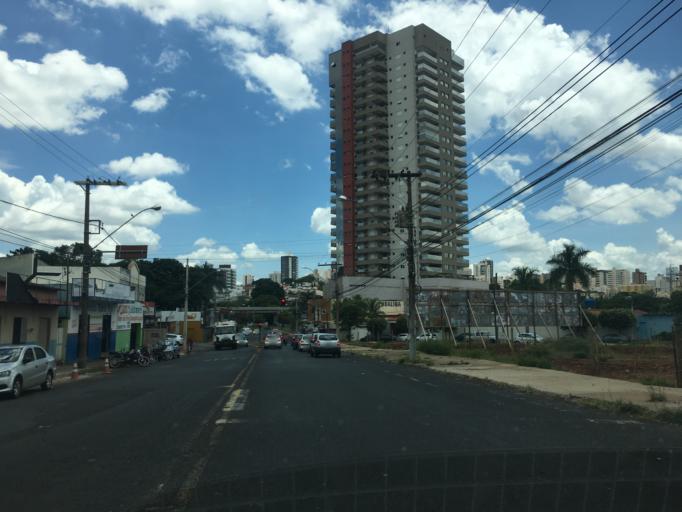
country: BR
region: Minas Gerais
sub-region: Uberlandia
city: Uberlandia
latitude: -18.9315
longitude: -48.2949
